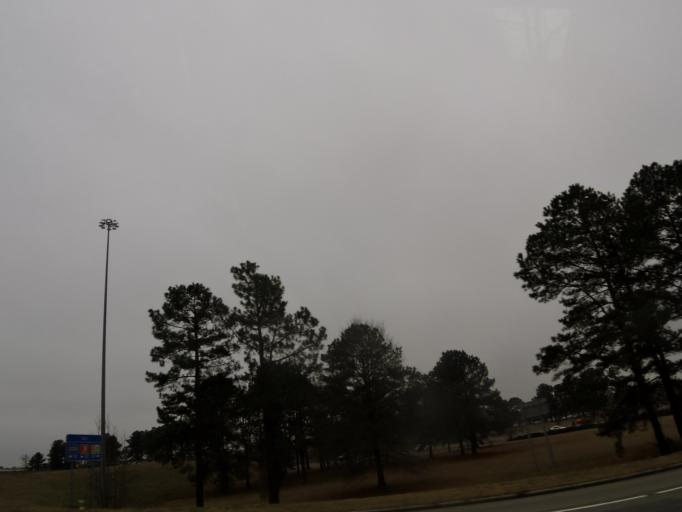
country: US
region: North Carolina
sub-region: Nash County
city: Rocky Mount
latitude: 35.9776
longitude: -77.8467
